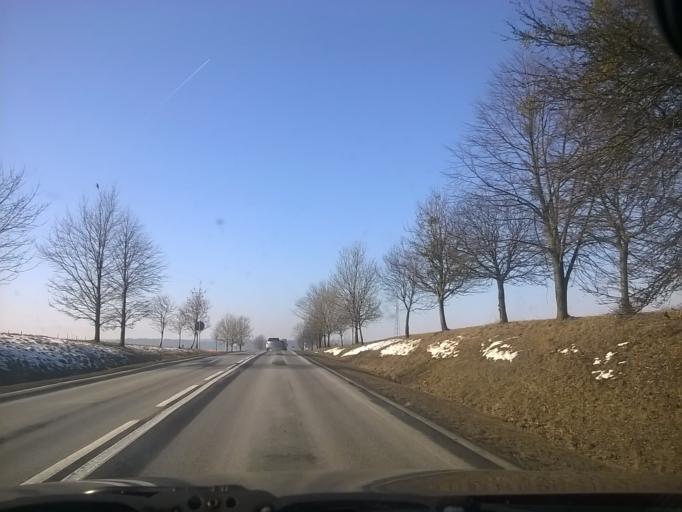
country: PL
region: Warmian-Masurian Voivodeship
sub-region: Powiat mragowski
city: Mragowo
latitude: 53.8421
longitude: 21.1627
